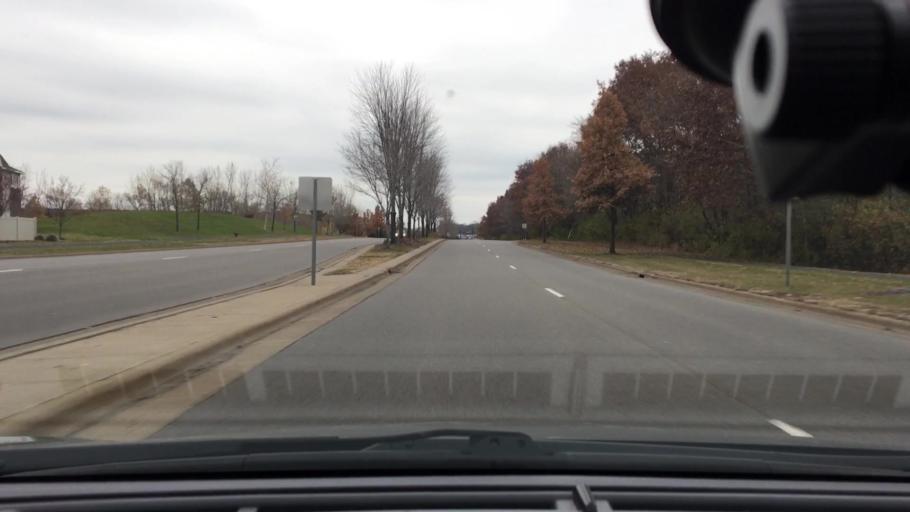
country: US
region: Minnesota
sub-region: Hennepin County
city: Maple Grove
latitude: 45.1198
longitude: -93.4924
